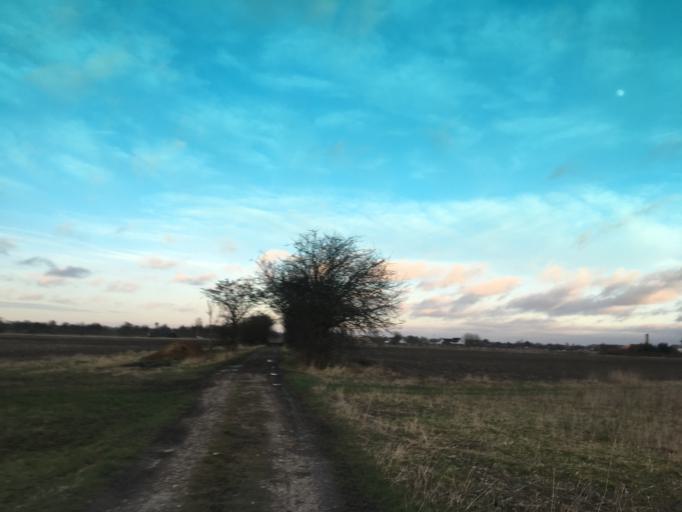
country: DK
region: Capital Region
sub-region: Dragor Kommune
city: Dragor
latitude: 55.5867
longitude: 12.6212
